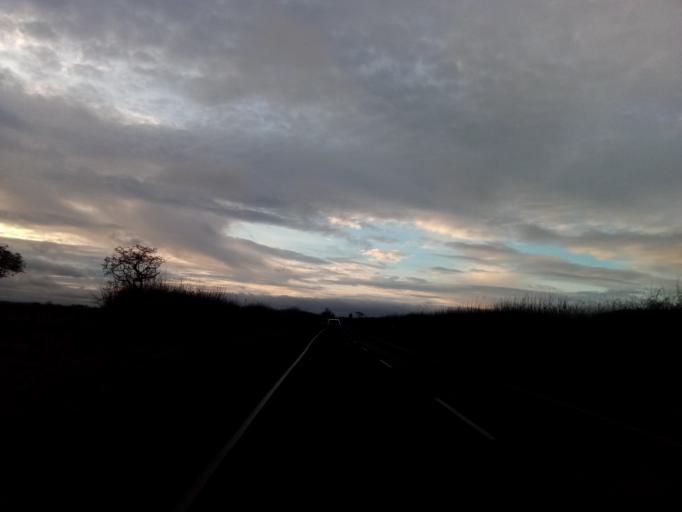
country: GB
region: England
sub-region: Newcastle upon Tyne
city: Dinnington
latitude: 55.0742
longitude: -1.7103
